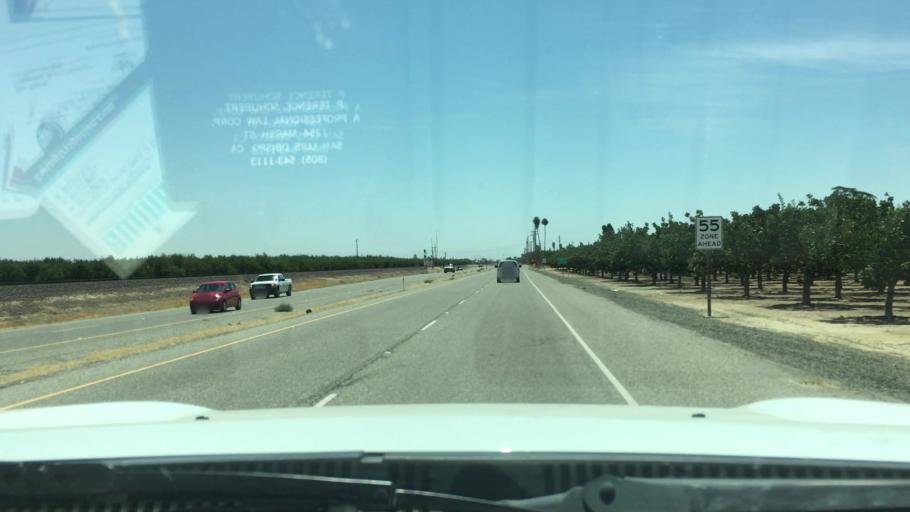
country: US
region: California
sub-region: Kern County
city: Shafter
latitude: 35.5187
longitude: -119.2936
